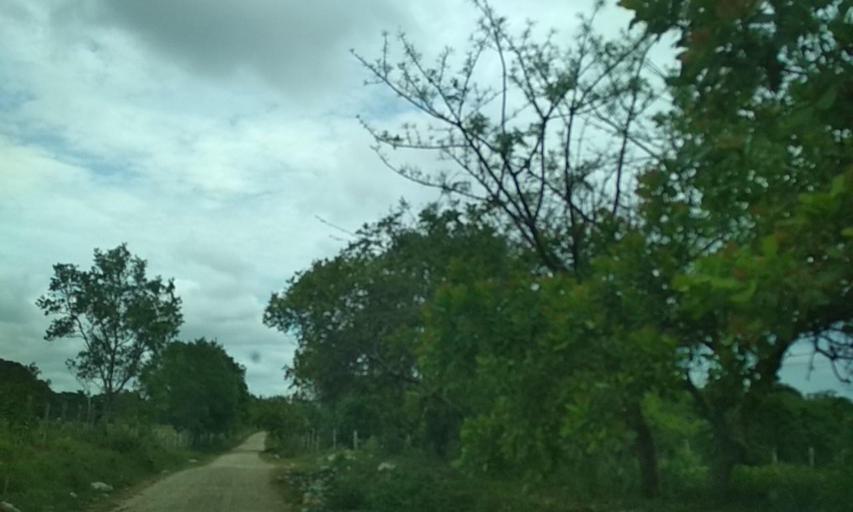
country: MX
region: Veracruz
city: Las Choapas
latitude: 17.8941
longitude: -94.1172
